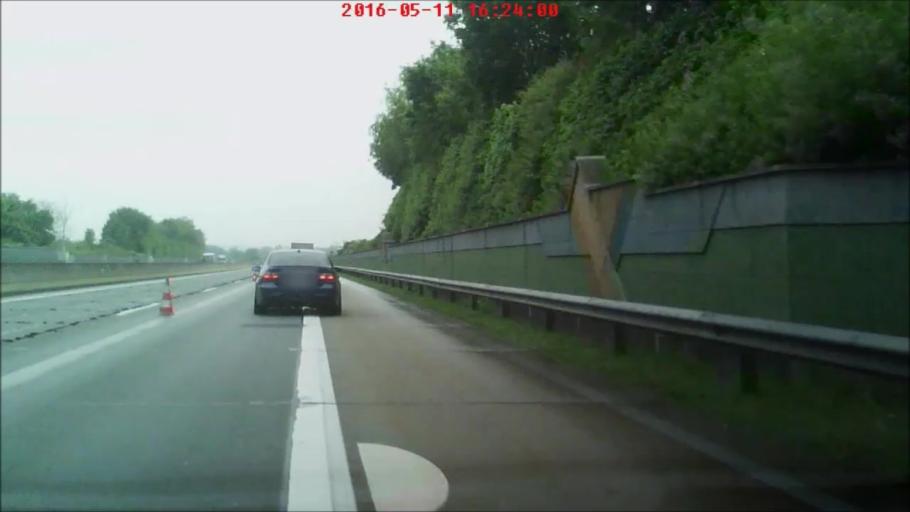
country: AT
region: Styria
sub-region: Politischer Bezirk Leibnitz
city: Obervogau
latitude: 46.7594
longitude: 15.5929
